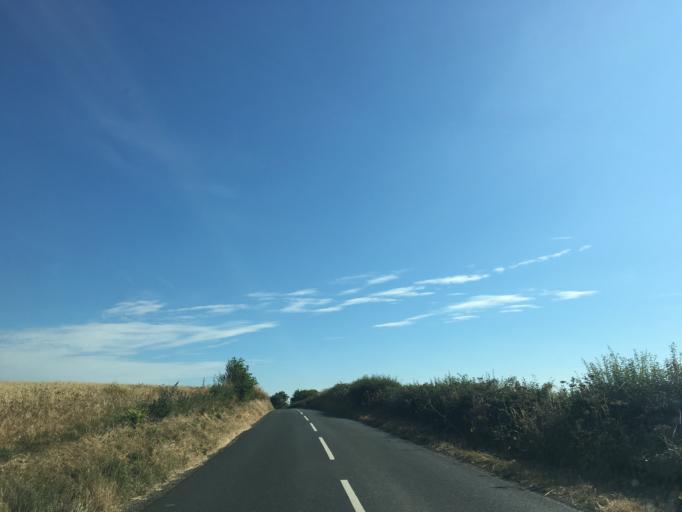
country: GB
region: England
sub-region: Isle of Wight
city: Chale
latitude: 50.6291
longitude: -1.3184
